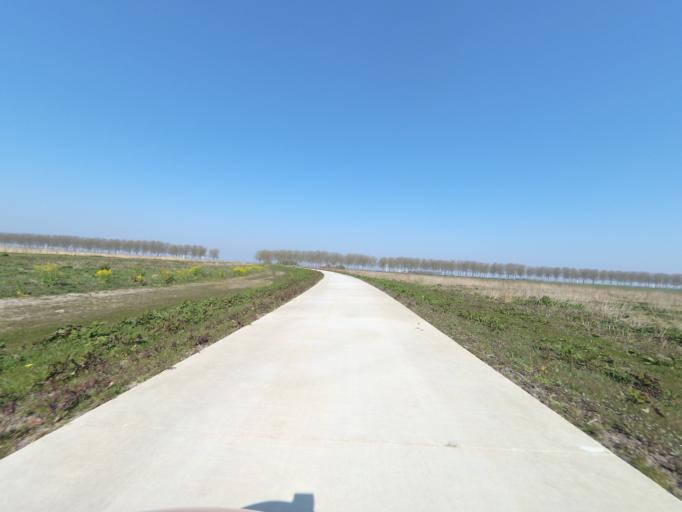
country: NL
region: Utrecht
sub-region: Gemeente Bunschoten
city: Spakenburg
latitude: 52.3623
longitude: 5.3848
